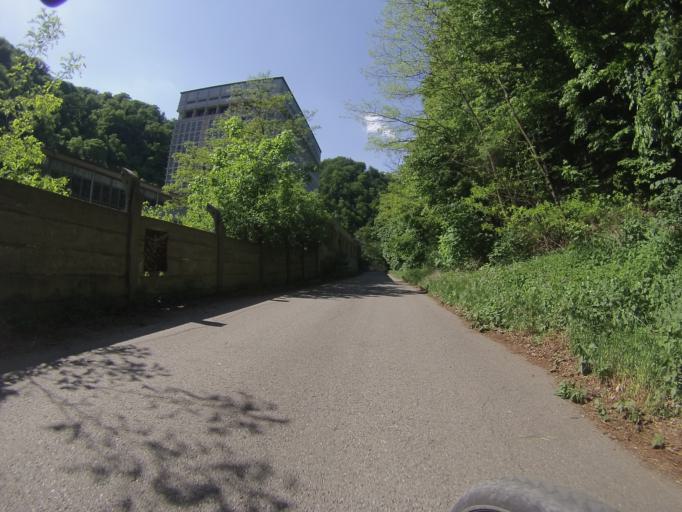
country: CZ
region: South Moravian
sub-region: Okres Blansko
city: Adamov
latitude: 49.3060
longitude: 16.6420
